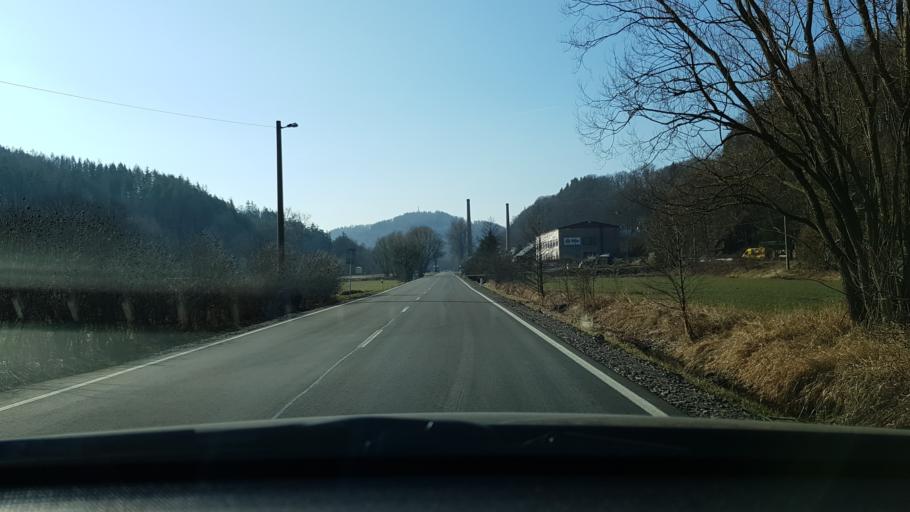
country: CZ
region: Olomoucky
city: Dolni Bohdikov
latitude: 49.9947
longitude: 16.8934
